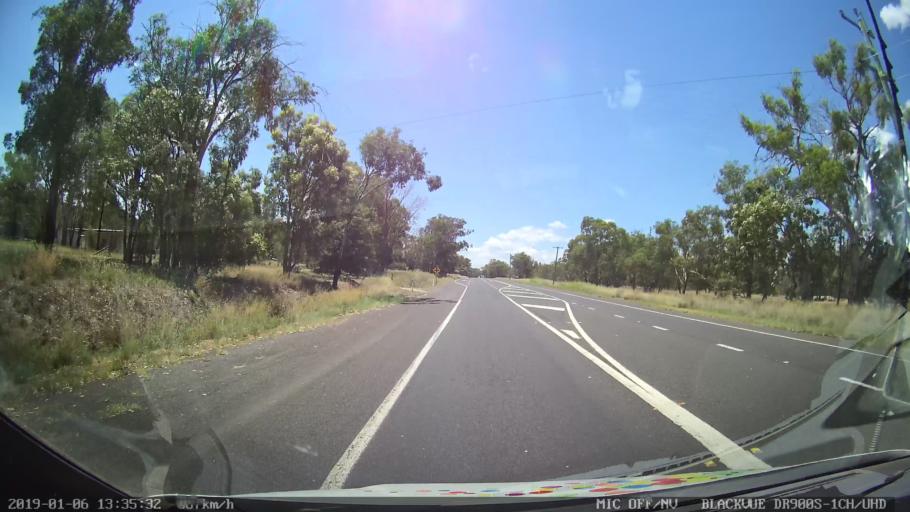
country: AU
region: New South Wales
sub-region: Tamworth Municipality
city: Kootingal
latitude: -31.0760
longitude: 151.0262
